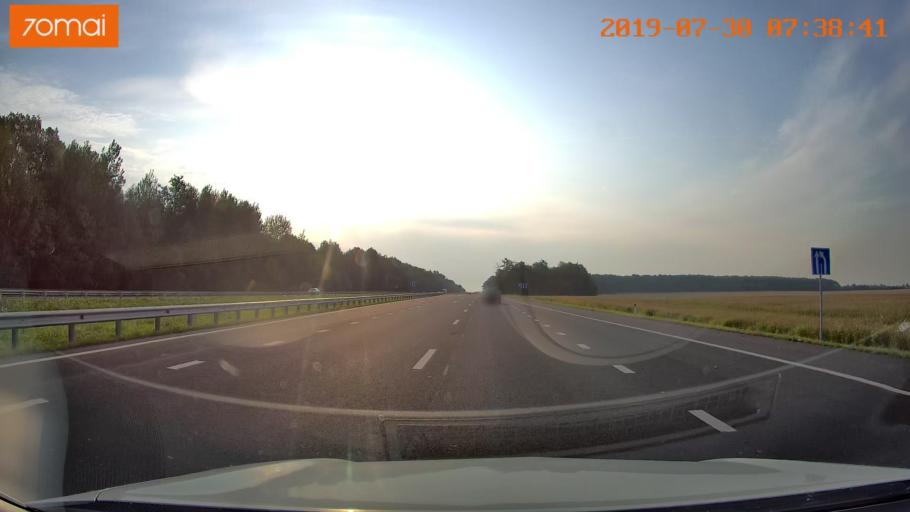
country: RU
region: Kaliningrad
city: Gvardeysk
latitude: 54.6497
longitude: 21.1753
